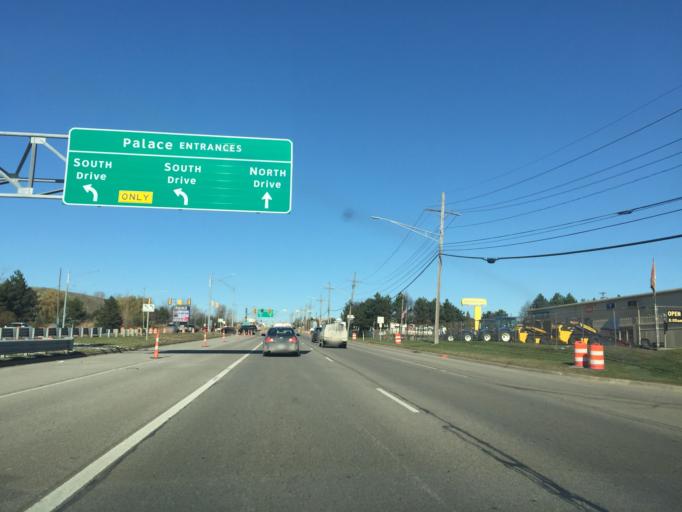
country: US
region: Michigan
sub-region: Oakland County
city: Auburn Hills
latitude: 42.6958
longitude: -83.2421
